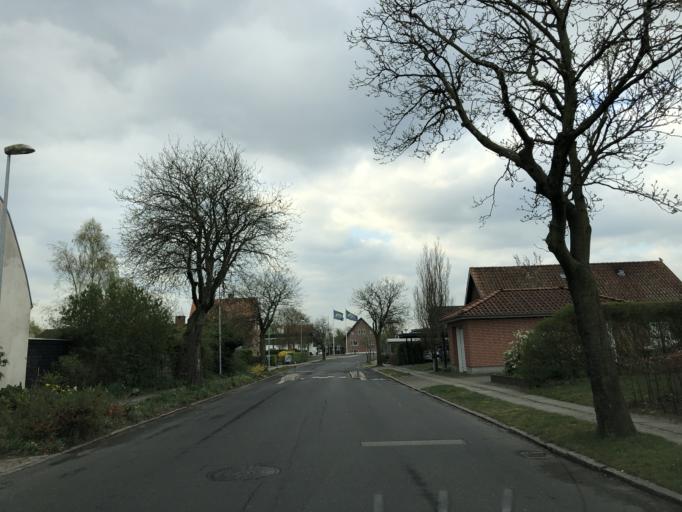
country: DK
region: Central Jutland
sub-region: Holstebro Kommune
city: Holstebro
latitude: 56.3608
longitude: 8.6336
